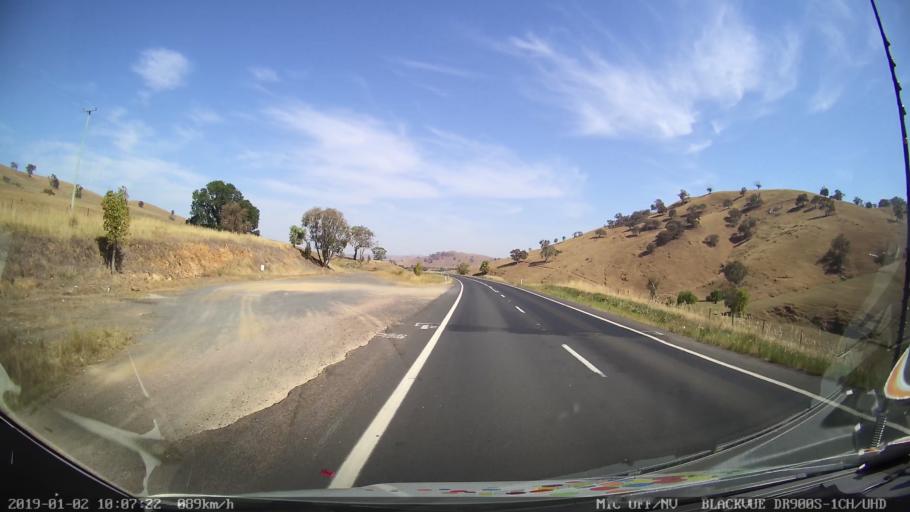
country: AU
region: New South Wales
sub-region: Gundagai
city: Gundagai
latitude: -35.1388
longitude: 148.1136
